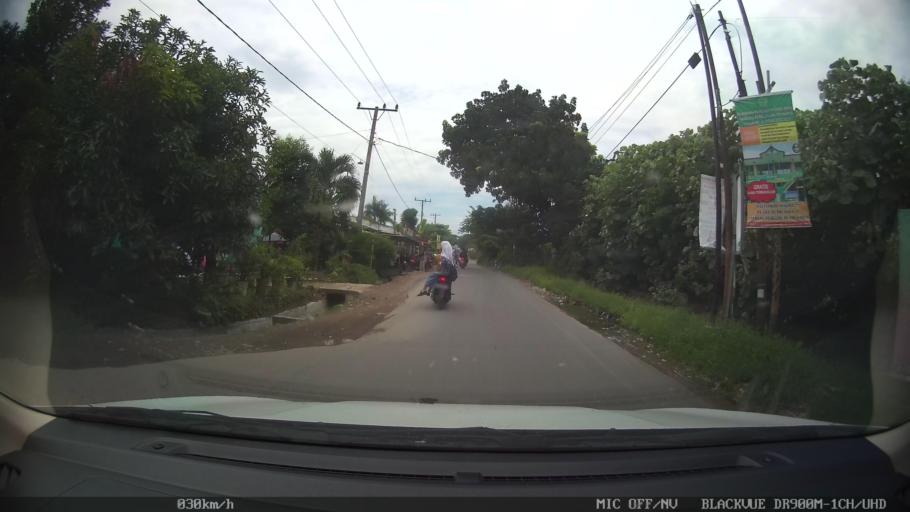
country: ID
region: North Sumatra
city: Sunggal
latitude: 3.6151
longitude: 98.5804
